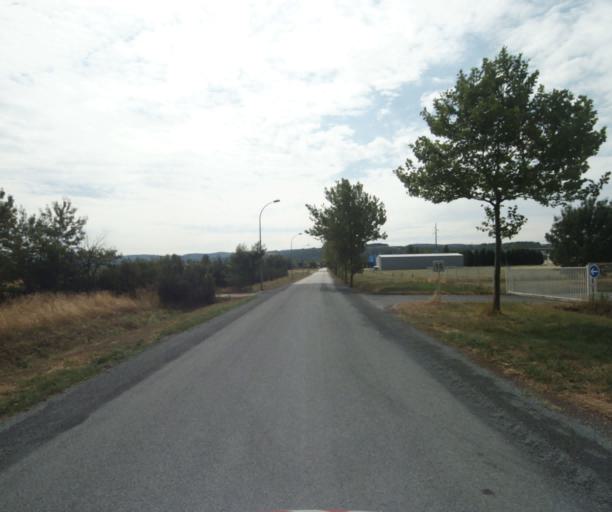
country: FR
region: Midi-Pyrenees
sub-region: Departement de la Haute-Garonne
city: Revel
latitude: 43.4583
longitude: 1.9829
